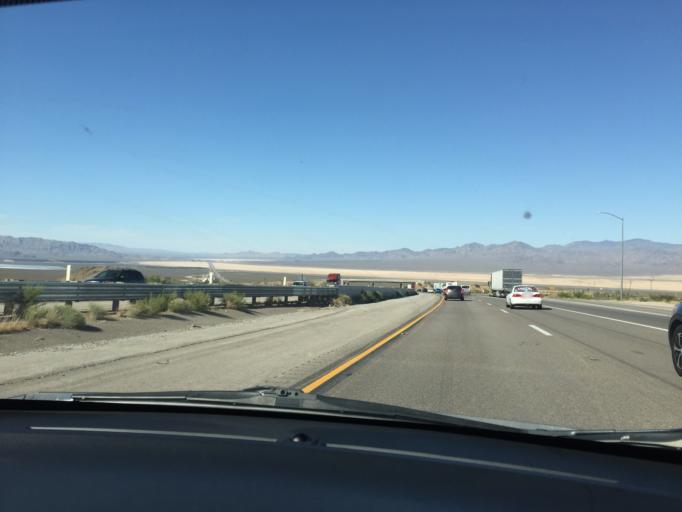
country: US
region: Nevada
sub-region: Clark County
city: Sandy Valley
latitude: 35.4698
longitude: -115.4520
